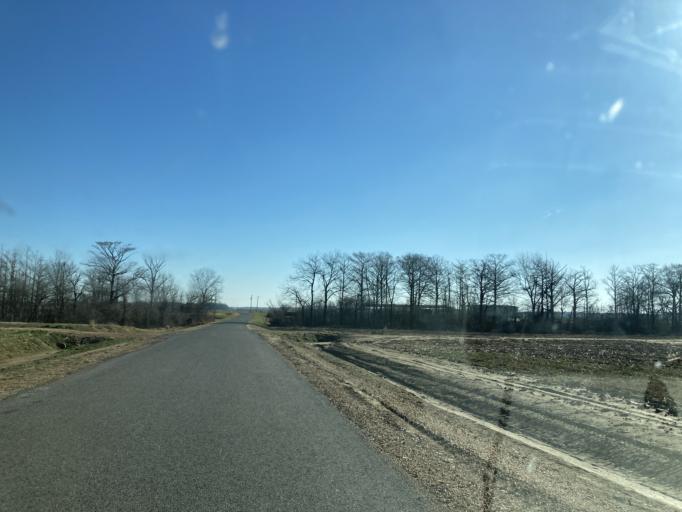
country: US
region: Mississippi
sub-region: Yazoo County
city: Yazoo City
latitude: 32.9519
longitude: -90.5942
